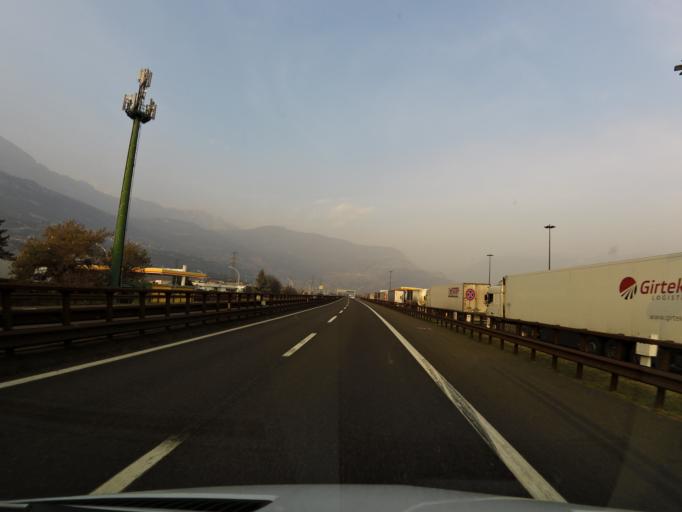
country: IT
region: Trentino-Alto Adige
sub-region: Provincia di Trento
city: Nogaredo
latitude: 45.9013
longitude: 11.0263
